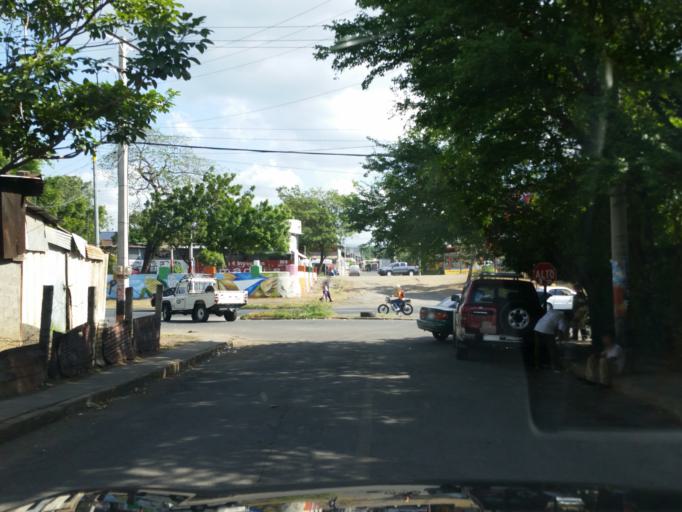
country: NI
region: Managua
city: Managua
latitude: 12.1546
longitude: -86.2626
